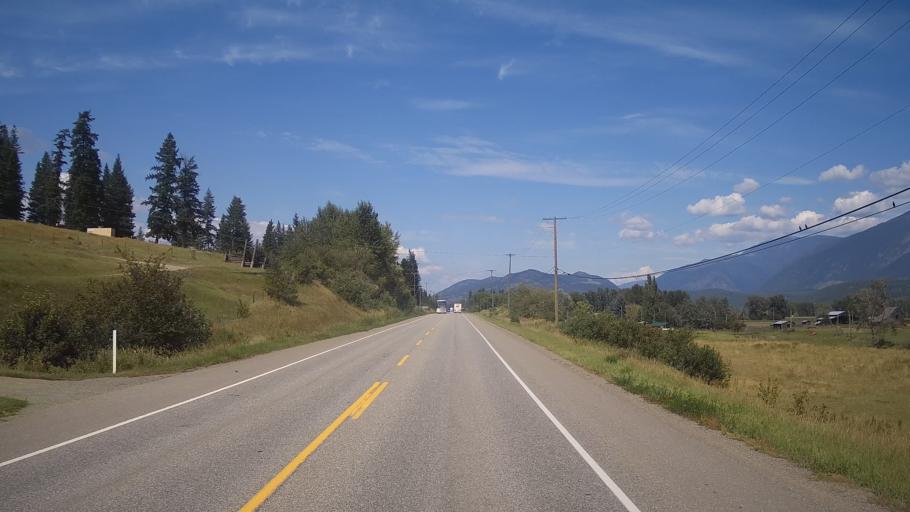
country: CA
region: British Columbia
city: Kamloops
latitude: 51.3042
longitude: -120.1816
